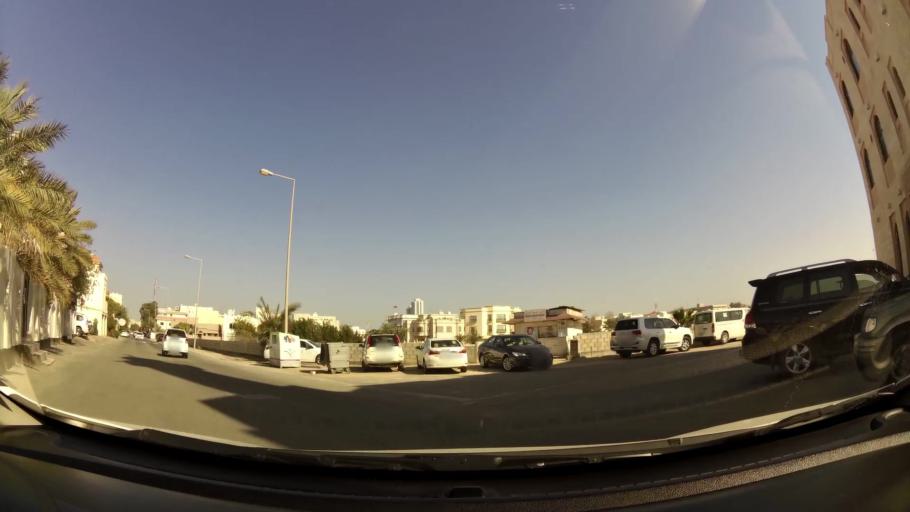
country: BH
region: Manama
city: Manama
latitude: 26.2082
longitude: 50.5684
